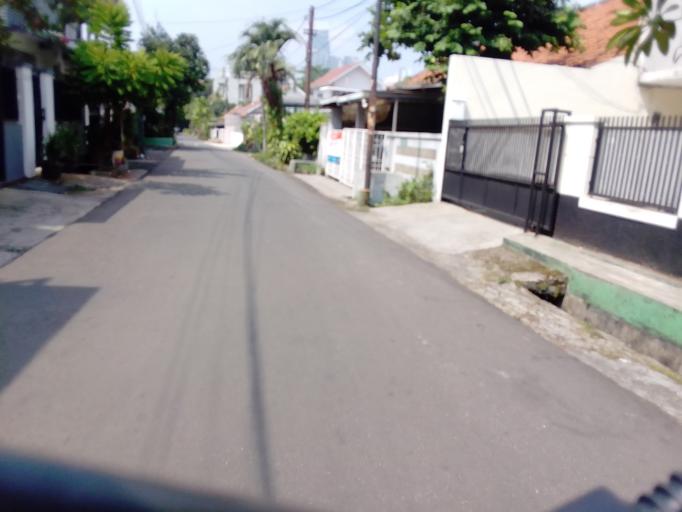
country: ID
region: Jakarta Raya
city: Jakarta
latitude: -6.2089
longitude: 106.8078
